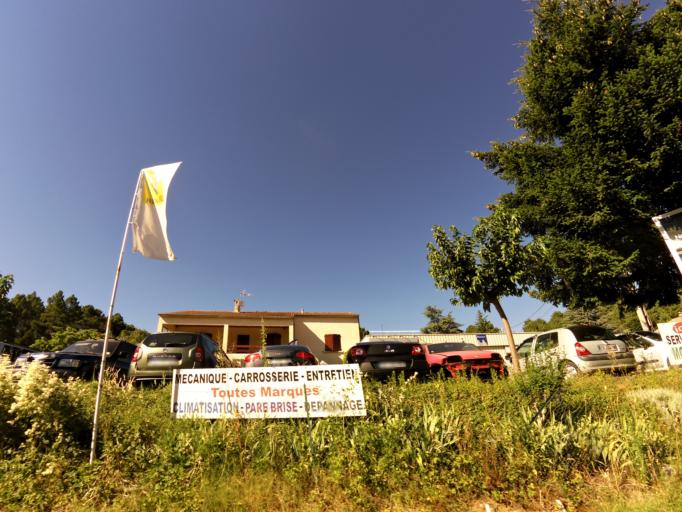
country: FR
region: Languedoc-Roussillon
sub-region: Departement du Gard
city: Saint-Jean-du-Gard
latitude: 44.1075
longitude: 3.8842
